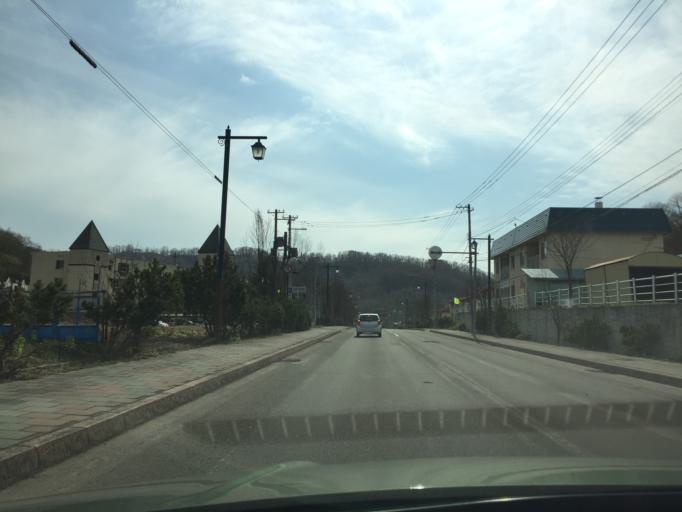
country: JP
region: Hokkaido
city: Utashinai
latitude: 43.5221
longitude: 142.0506
